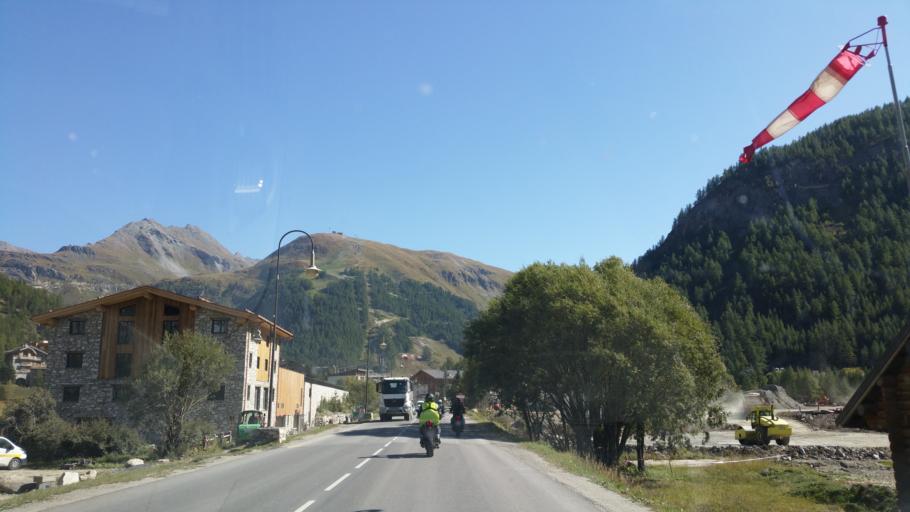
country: FR
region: Rhone-Alpes
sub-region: Departement de la Savoie
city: Val-d'Isere
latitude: 45.4573
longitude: 6.9681
